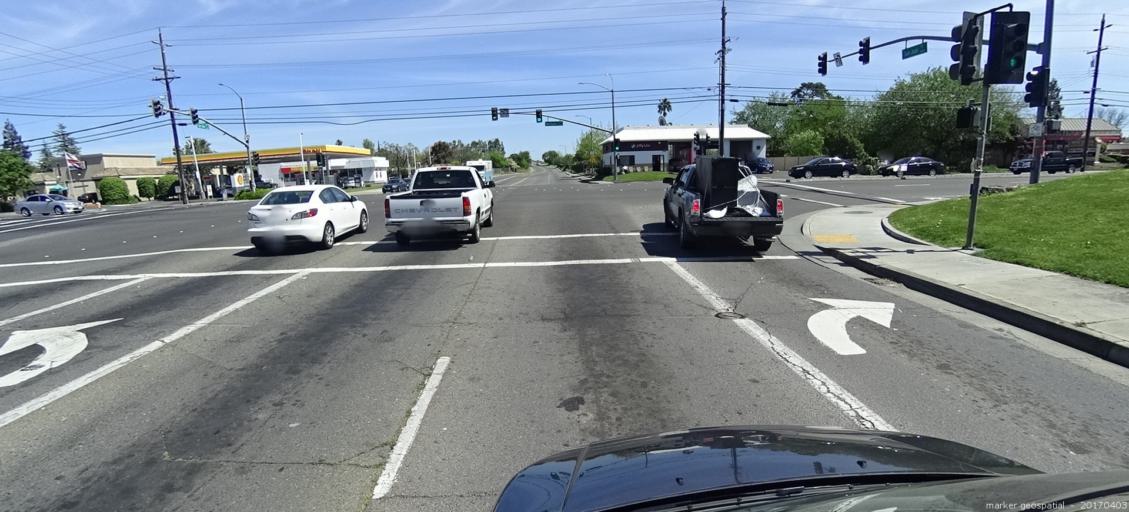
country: US
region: California
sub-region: Sacramento County
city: Sacramento
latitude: 38.6296
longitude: -121.4760
